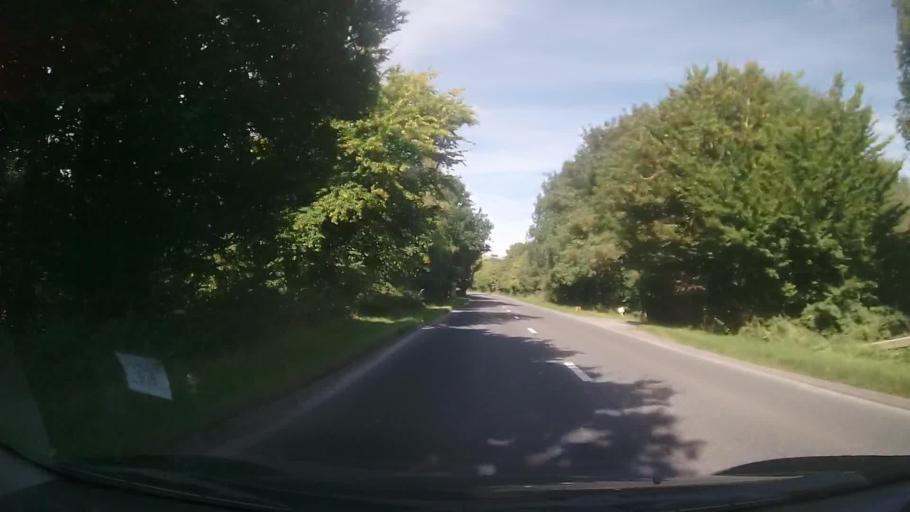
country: GB
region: England
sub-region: Herefordshire
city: Kington
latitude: 52.2031
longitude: -3.0205
